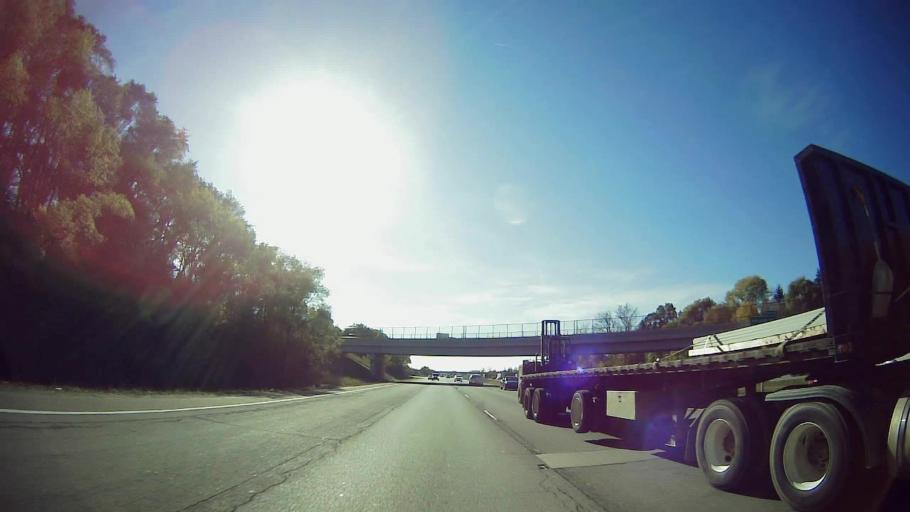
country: US
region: Michigan
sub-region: Wayne County
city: Plymouth
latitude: 42.3632
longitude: -83.4358
